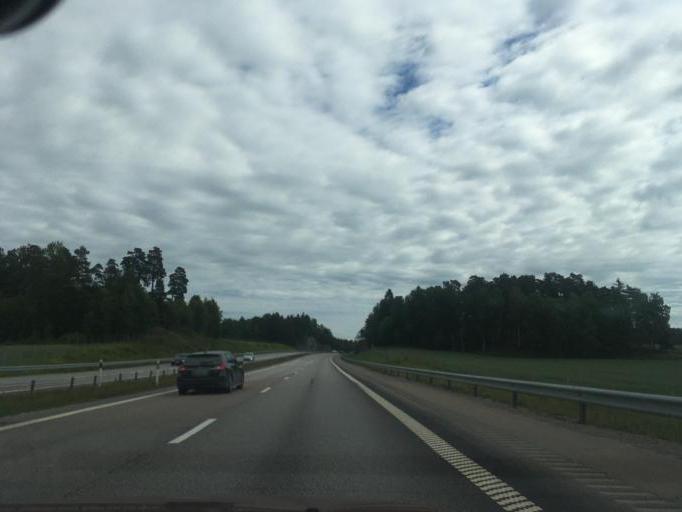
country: SE
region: Soedermanland
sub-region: Nykopings Kommun
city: Nykoping
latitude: 58.7934
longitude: 17.0874
